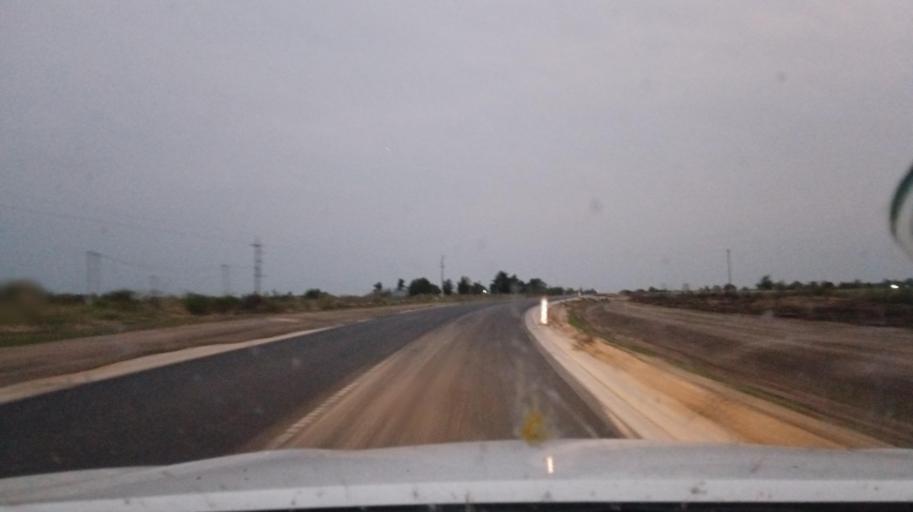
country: UY
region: Canelones
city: Sauce
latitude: -34.5738
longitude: -56.1007
